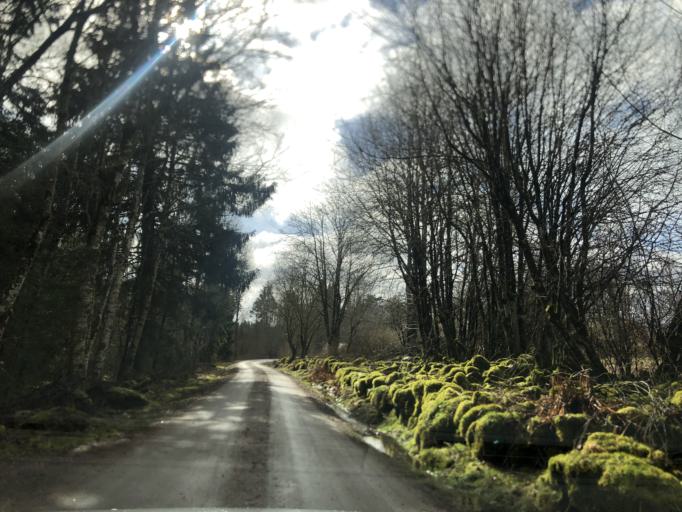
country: SE
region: Vaestra Goetaland
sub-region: Boras Kommun
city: Dalsjofors
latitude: 57.8264
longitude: 13.2210
